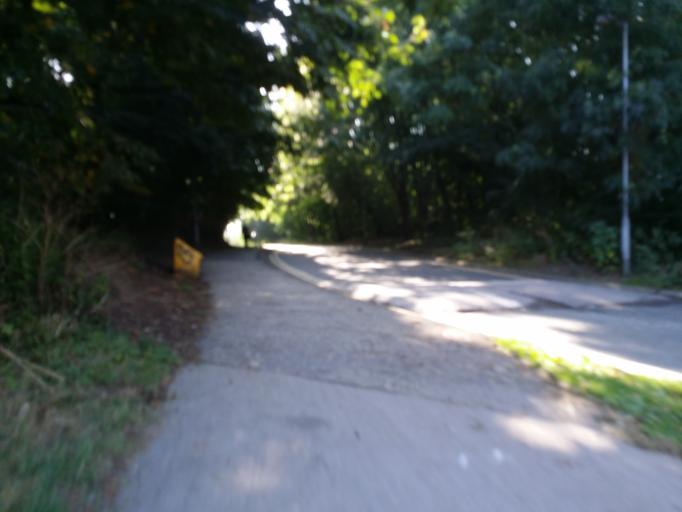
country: GB
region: England
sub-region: City of York
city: Heslington
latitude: 53.9503
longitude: -1.0557
